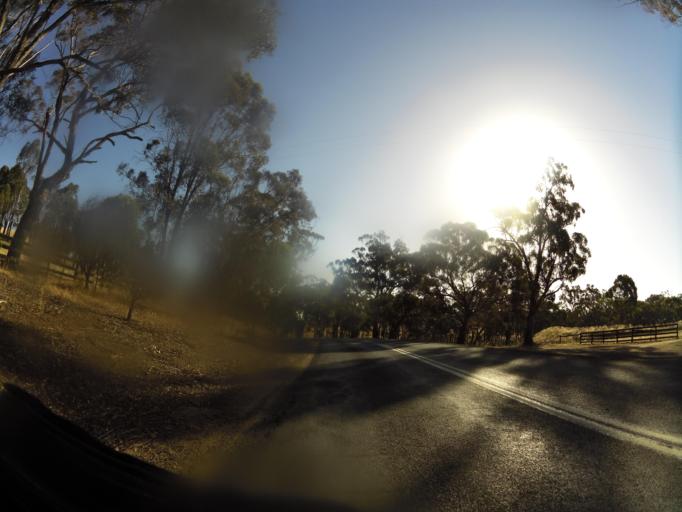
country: AU
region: Victoria
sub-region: Murrindindi
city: Kinglake West
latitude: -37.0119
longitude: 145.1194
